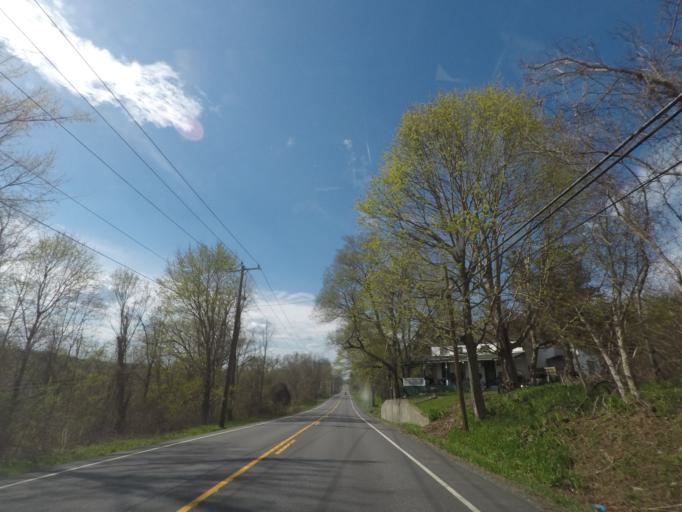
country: US
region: New York
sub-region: Greene County
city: Cairo
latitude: 42.3359
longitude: -74.0221
